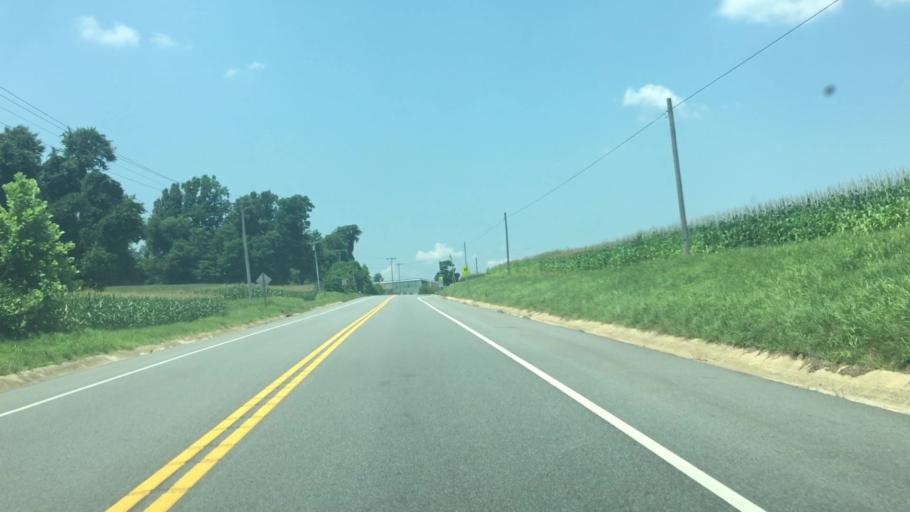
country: US
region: Maryland
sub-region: Saint Mary's County
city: Mechanicsville
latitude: 38.3786
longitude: -76.7119
